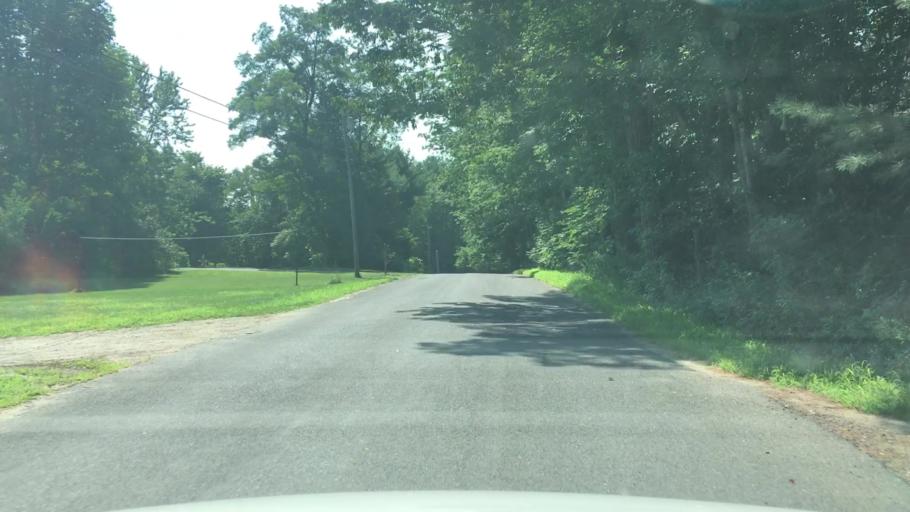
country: US
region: Maine
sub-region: Androscoggin County
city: Greene
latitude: 44.2241
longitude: -70.1051
